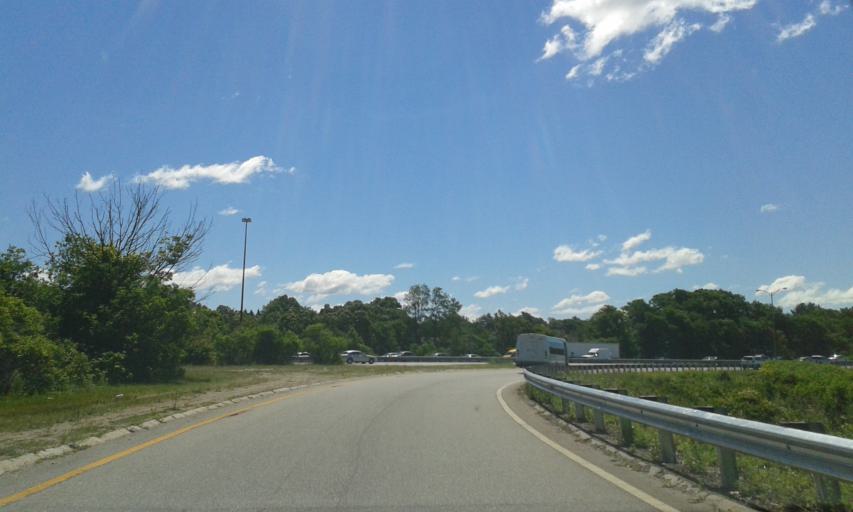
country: US
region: Massachusetts
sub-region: Middlesex County
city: Stoneham
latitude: 42.5006
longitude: -71.1196
